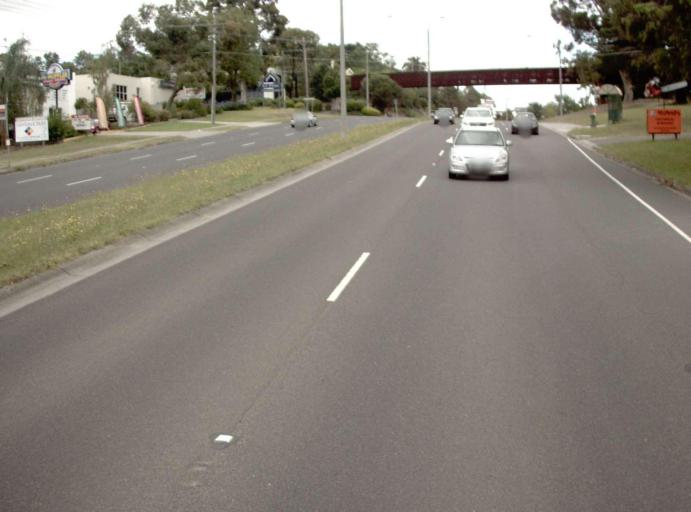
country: AU
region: Victoria
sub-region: Yarra Ranges
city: Lilydale
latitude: -37.7558
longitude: 145.3610
